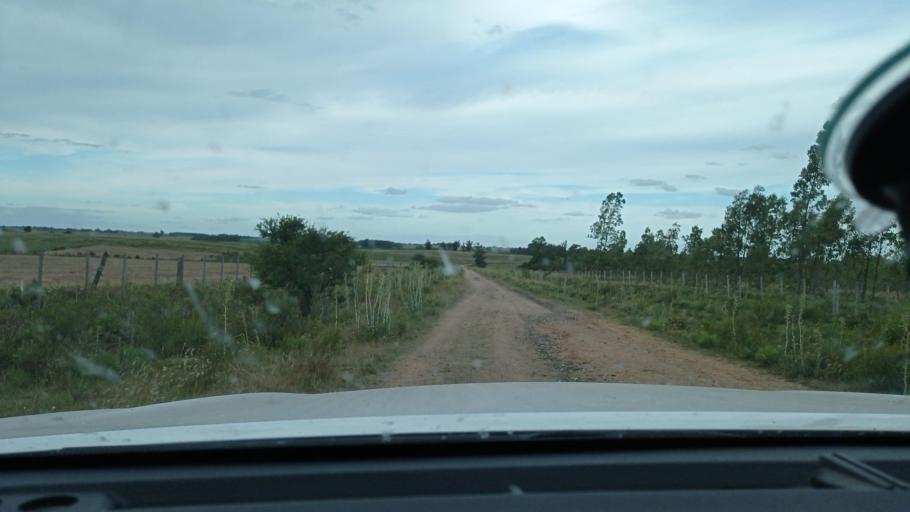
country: UY
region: Florida
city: Casupa
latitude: -34.1240
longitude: -55.8110
